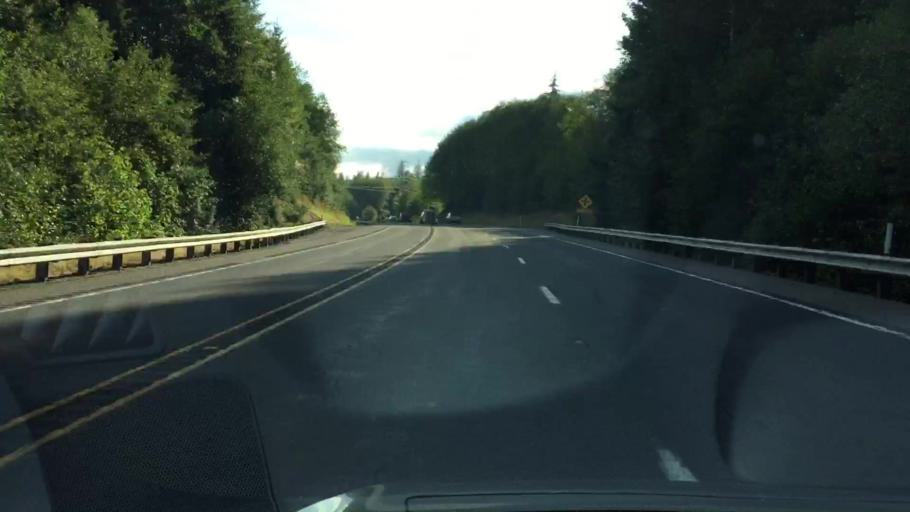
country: US
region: Washington
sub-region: Lewis County
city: Morton
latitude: 46.5464
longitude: -122.3426
